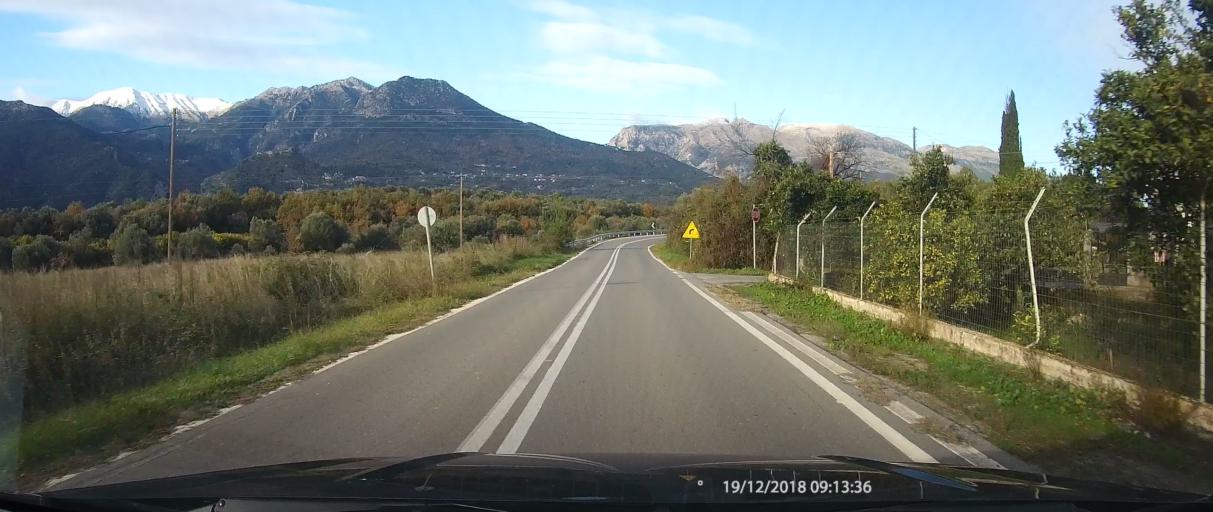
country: GR
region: Peloponnese
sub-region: Nomos Lakonias
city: Magoula
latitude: 37.0813
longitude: 22.3957
